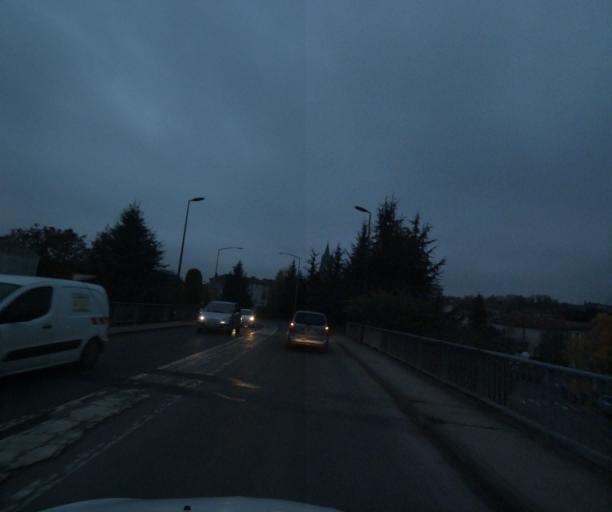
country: FR
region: Poitou-Charentes
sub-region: Departement de la Charente-Maritime
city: Saintes
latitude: 45.7418
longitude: -0.6367
